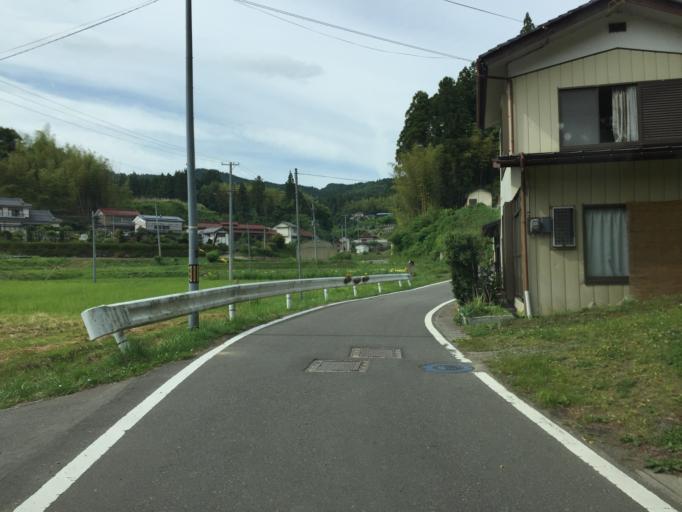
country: JP
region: Fukushima
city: Funehikimachi-funehiki
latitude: 37.4554
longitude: 140.6410
